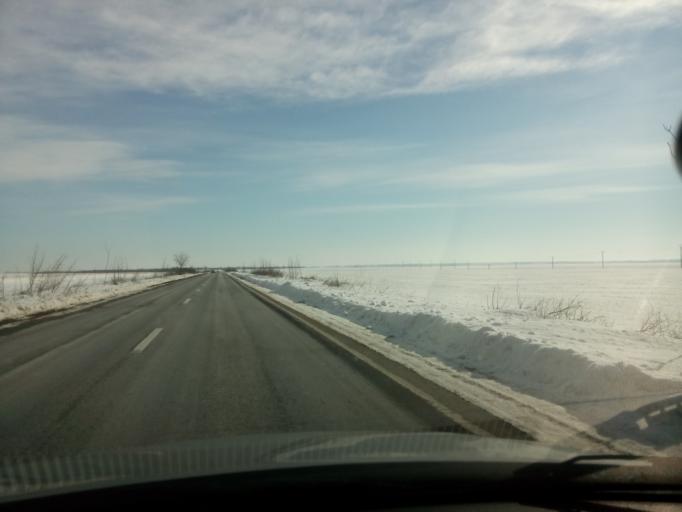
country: RO
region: Giurgiu
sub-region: Comuna Herasti
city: Herasti
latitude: 44.2441
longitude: 26.3839
